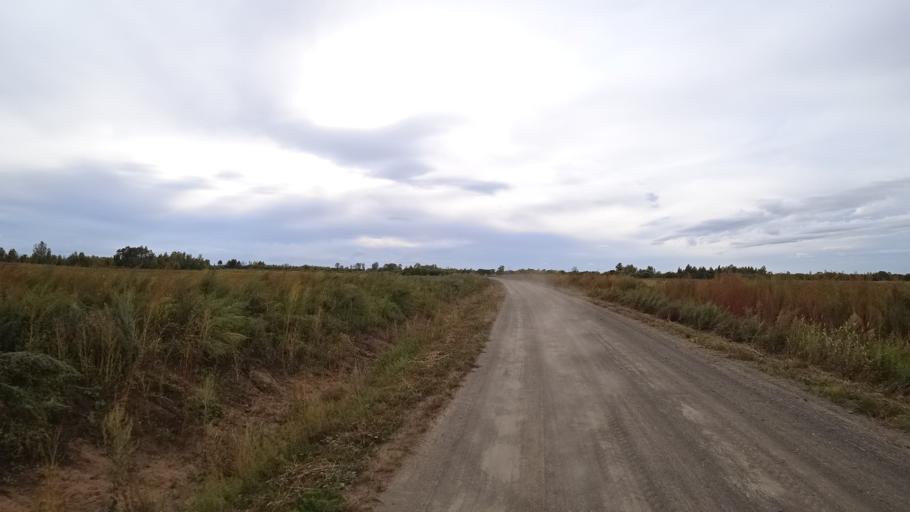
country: RU
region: Amur
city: Arkhara
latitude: 49.3537
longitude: 130.1420
